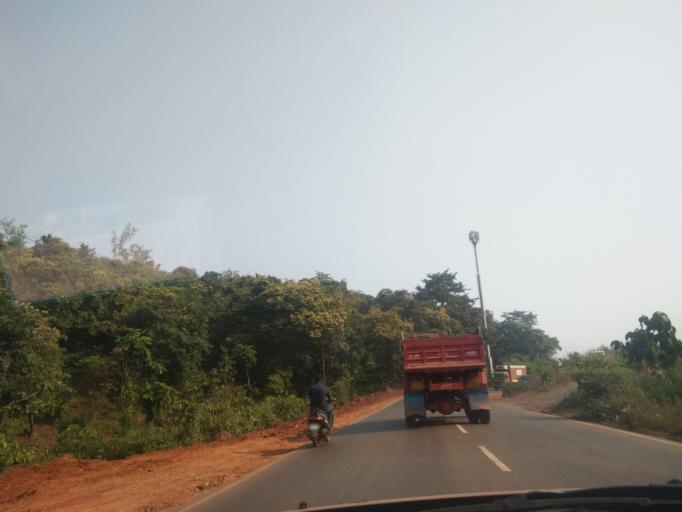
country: IN
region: Goa
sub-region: North Goa
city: Curti
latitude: 15.4150
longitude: 74.0347
